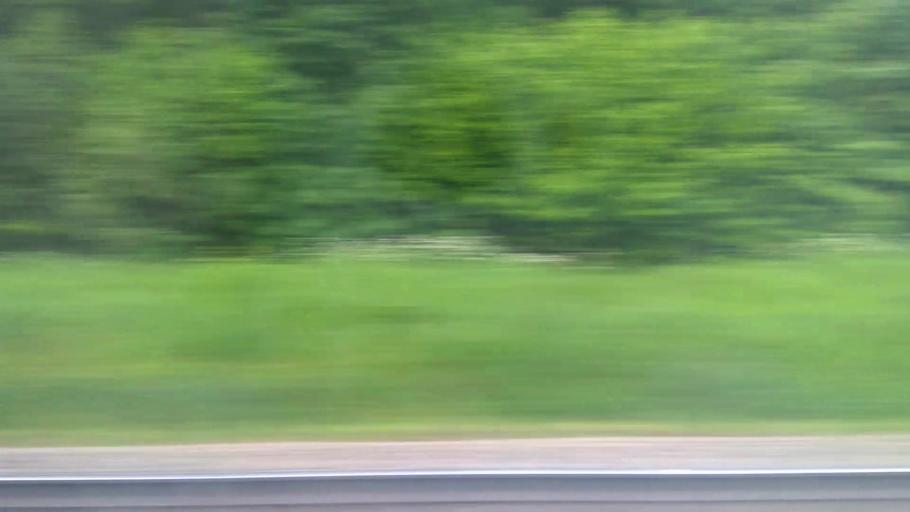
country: RU
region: Moskovskaya
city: Il'inskoye
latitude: 55.2072
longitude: 37.9198
